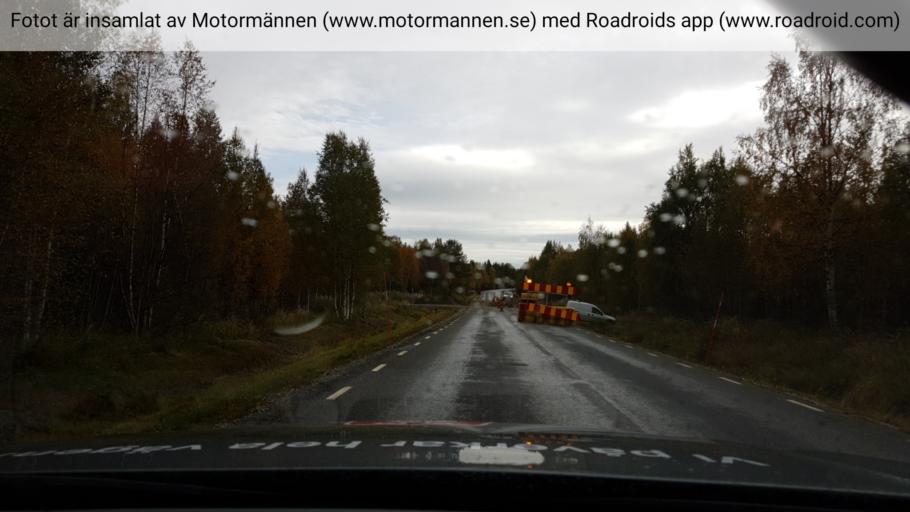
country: SE
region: Vaesterbotten
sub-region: Vilhelmina Kommun
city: Sjoberg
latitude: 64.7647
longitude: 16.1516
